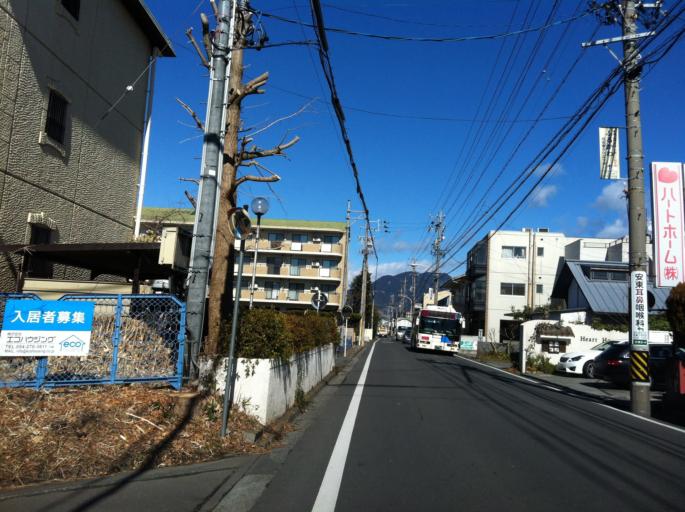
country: JP
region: Shizuoka
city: Shizuoka-shi
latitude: 34.9880
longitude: 138.3860
